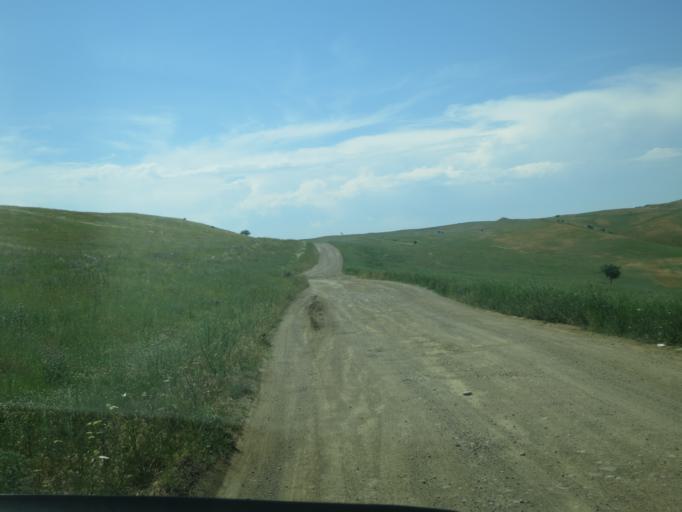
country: AZ
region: Agstafa
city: Saloglu
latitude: 41.4672
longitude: 45.3291
